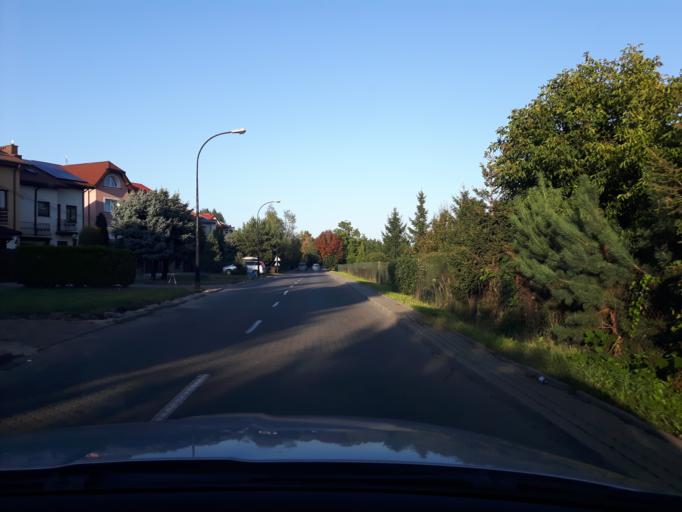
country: PL
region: Masovian Voivodeship
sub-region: Powiat wolominski
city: Zabki
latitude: 52.2792
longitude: 21.0794
